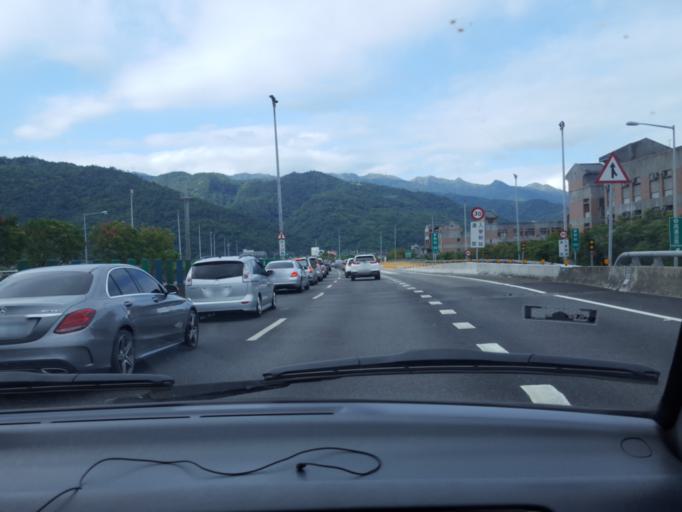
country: TW
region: Taiwan
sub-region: Yilan
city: Yilan
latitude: 24.8320
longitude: 121.7909
